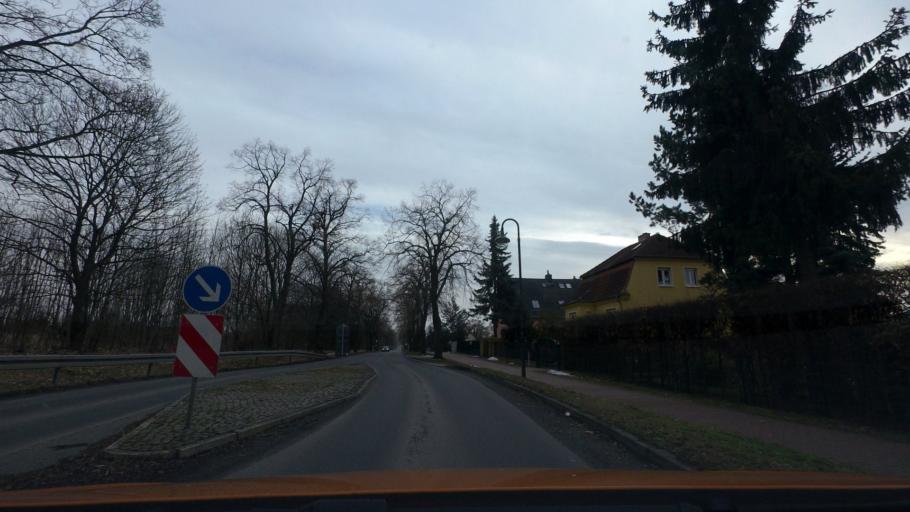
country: DE
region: Brandenburg
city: Ahrensfelde
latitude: 52.5826
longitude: 13.5673
